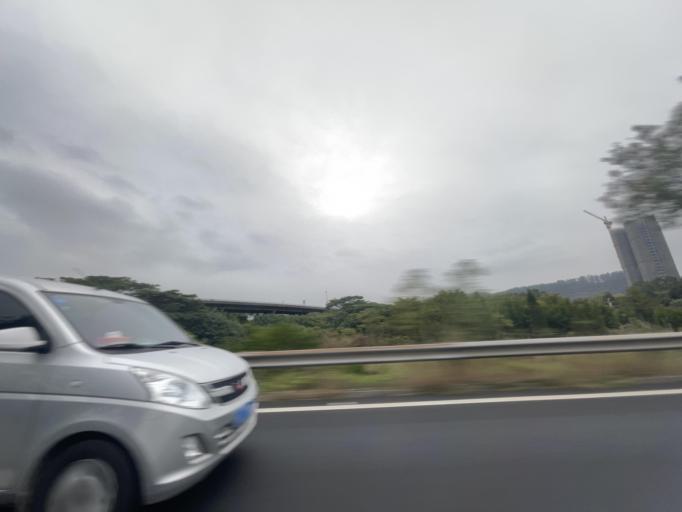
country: CN
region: Guangdong
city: Huangge
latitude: 22.7902
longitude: 113.5044
